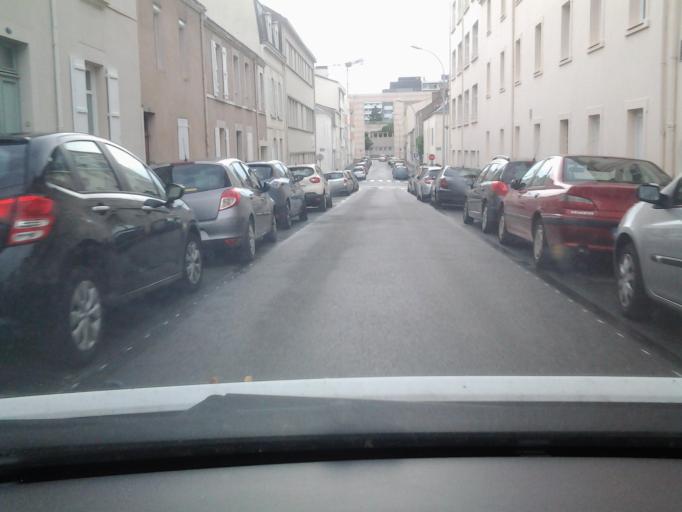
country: FR
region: Pays de la Loire
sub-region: Departement de la Vendee
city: La Roche-sur-Yon
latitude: 46.6729
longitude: -1.4265
